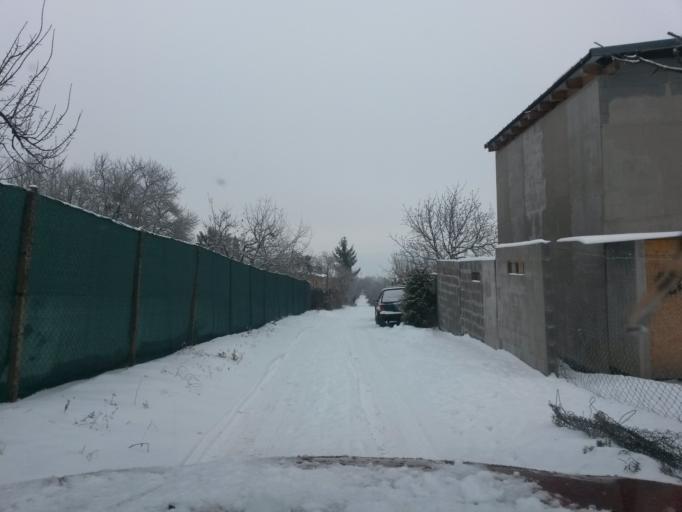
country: SK
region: Kosicky
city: Kosice
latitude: 48.7165
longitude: 21.3131
